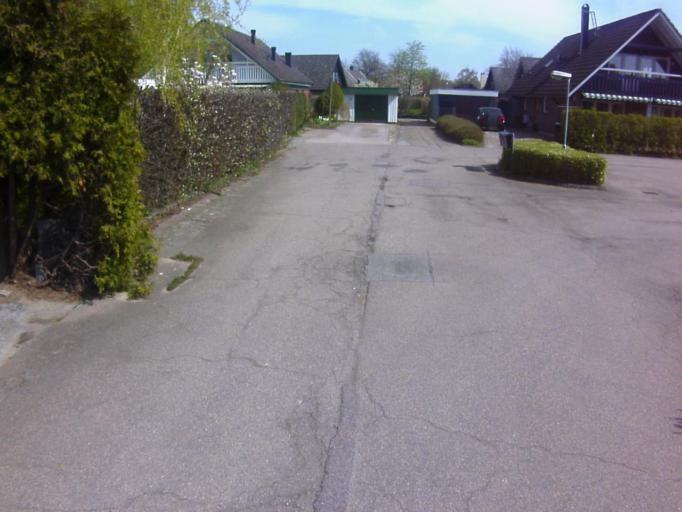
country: SE
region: Skane
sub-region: Kavlinge Kommun
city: Loddekopinge
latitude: 55.7646
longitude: 13.0066
